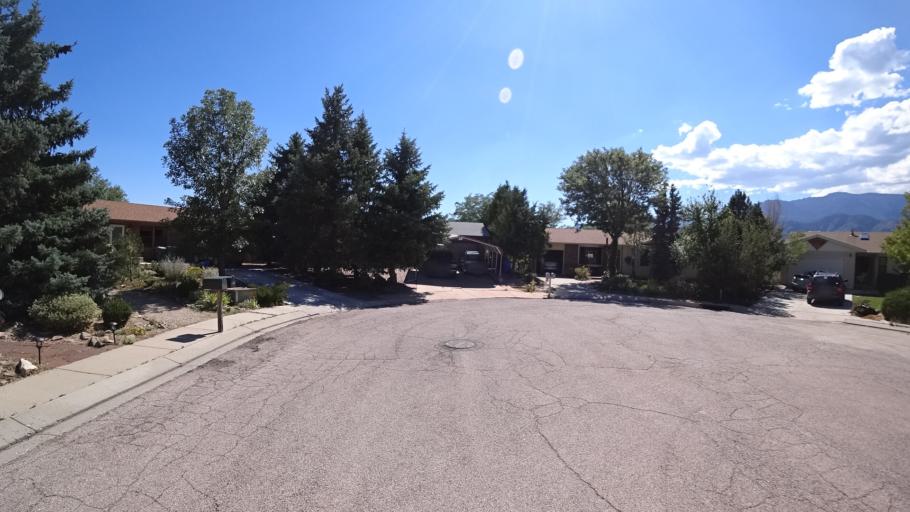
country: US
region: Colorado
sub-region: El Paso County
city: Colorado Springs
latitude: 38.8541
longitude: -104.8536
